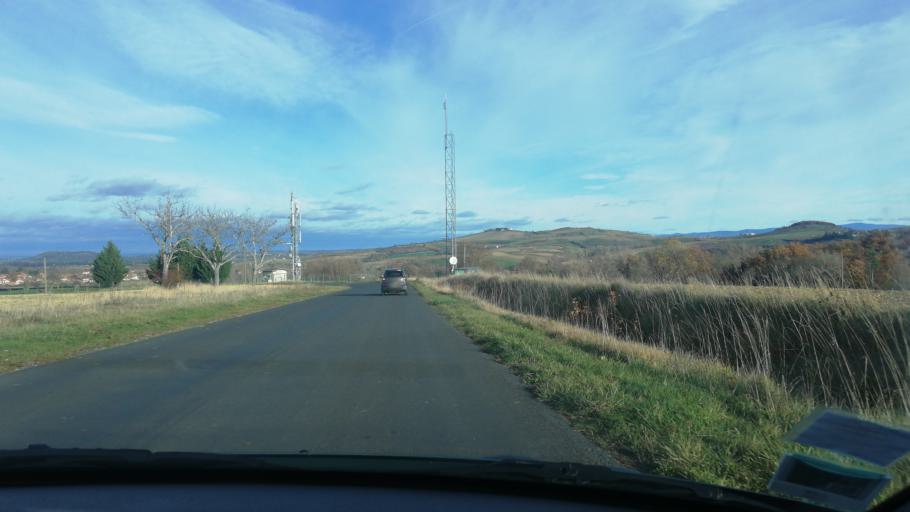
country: FR
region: Auvergne
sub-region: Departement du Puy-de-Dome
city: Billom
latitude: 45.7090
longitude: 3.3519
